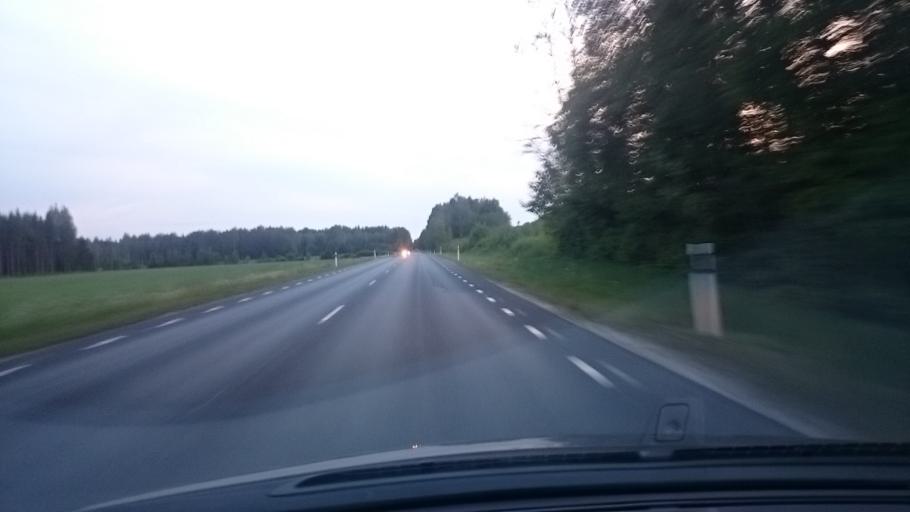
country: EE
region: Paernumaa
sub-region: Vaendra vald (alev)
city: Vandra
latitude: 58.8397
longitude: 25.0686
